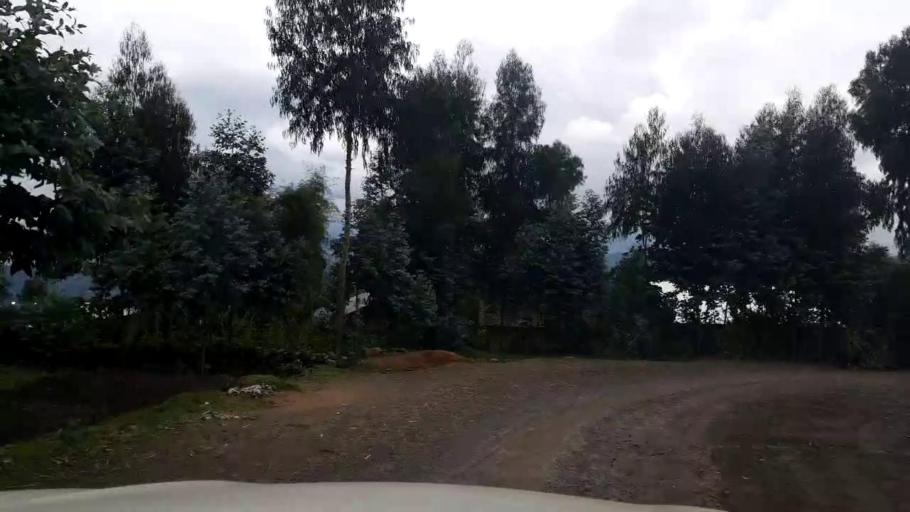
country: RW
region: Northern Province
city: Musanze
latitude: -1.5386
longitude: 29.5344
